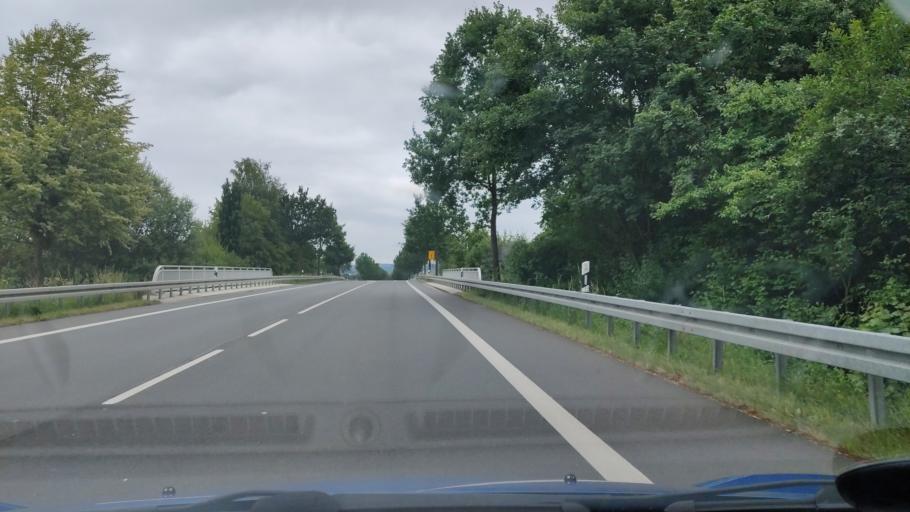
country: DE
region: Lower Saxony
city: Dielmissen
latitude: 51.9613
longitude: 9.6033
